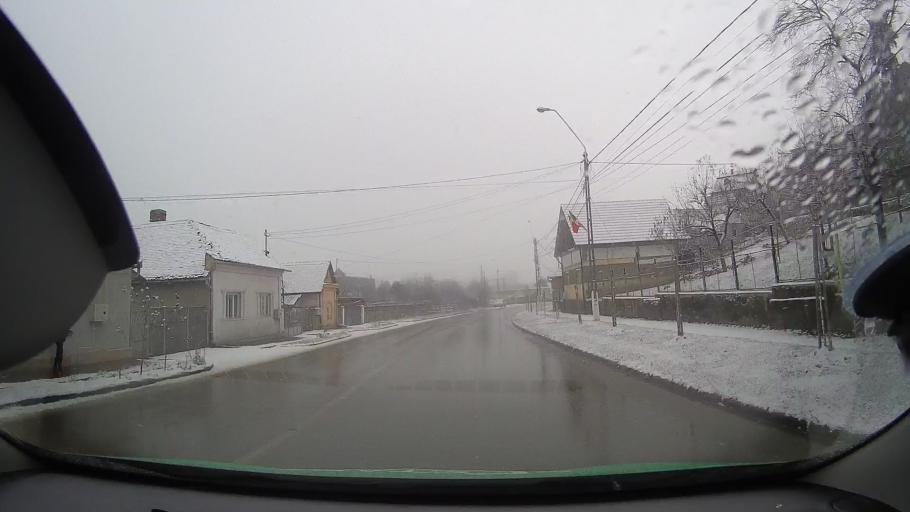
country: RO
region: Alba
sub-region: Municipiul Aiud
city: Aiud
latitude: 46.3106
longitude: 23.7334
